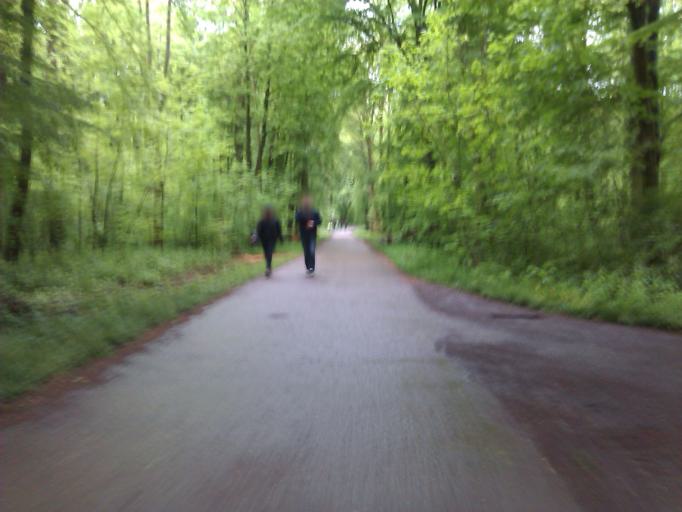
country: DE
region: Baden-Wuerttemberg
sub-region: Karlsruhe Region
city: Karlsruhe
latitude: 48.9898
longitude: 8.4190
